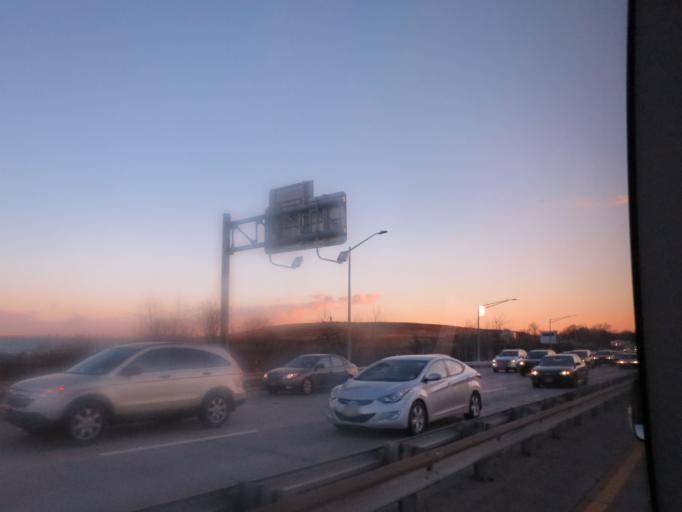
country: US
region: New York
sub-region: Kings County
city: East New York
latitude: 40.6457
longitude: -73.8745
